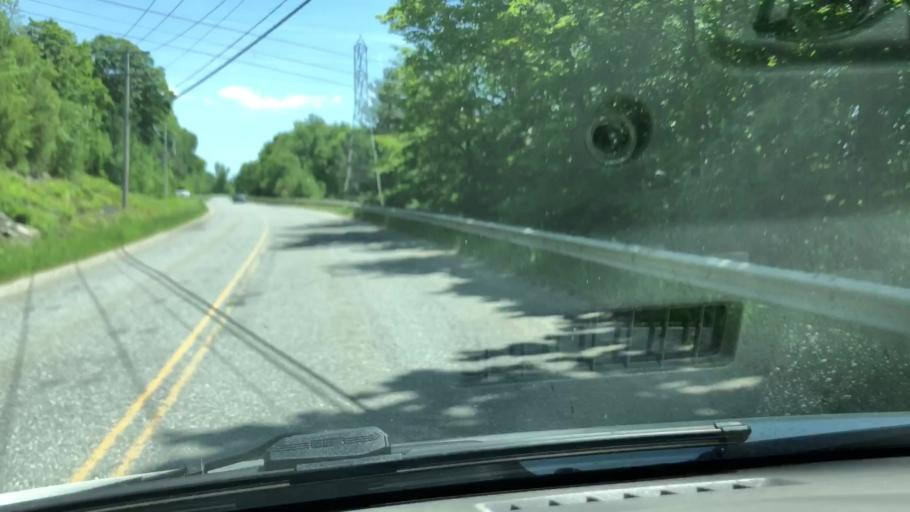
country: US
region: Massachusetts
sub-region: Franklin County
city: Charlemont
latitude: 42.5199
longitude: -72.9252
